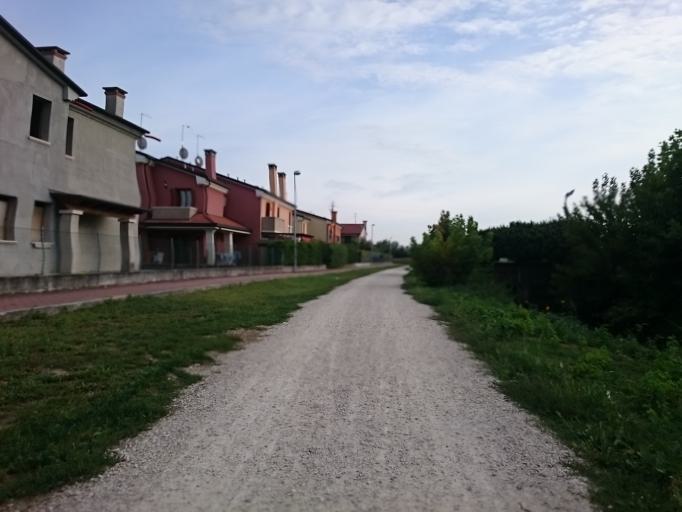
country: IT
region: Veneto
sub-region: Provincia di Vicenza
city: Camisano Vicentino
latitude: 45.5384
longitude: 11.6877
